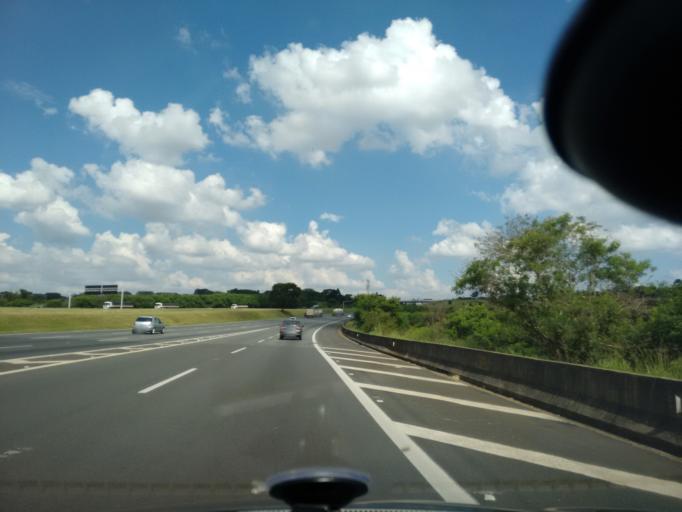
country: BR
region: Sao Paulo
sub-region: Campinas
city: Campinas
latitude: -22.9241
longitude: -47.1317
